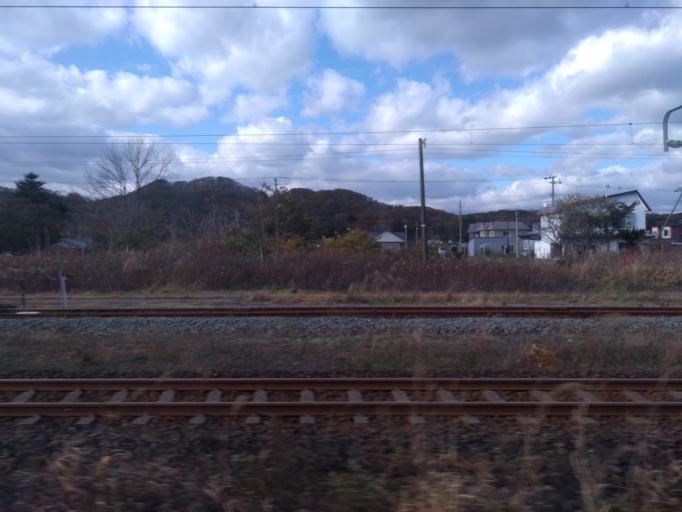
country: JP
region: Hokkaido
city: Shiraoi
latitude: 42.4949
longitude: 141.2635
